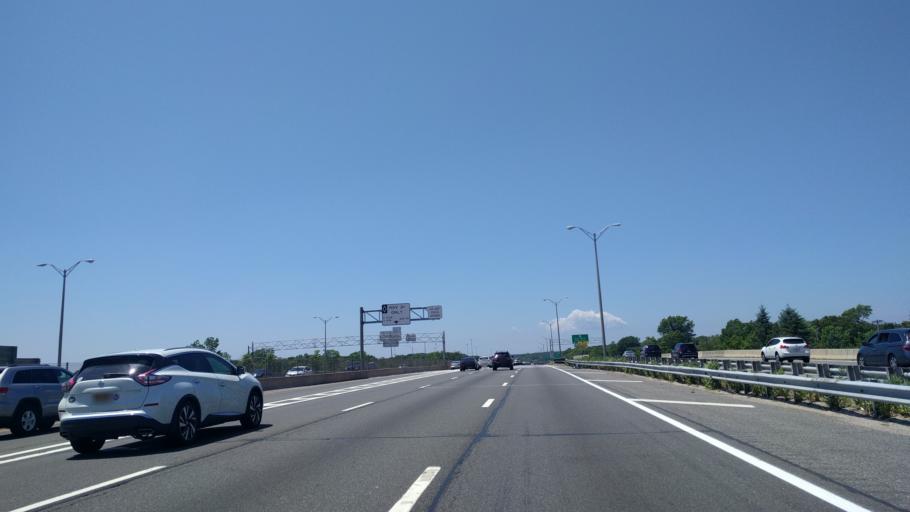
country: US
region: New York
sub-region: Suffolk County
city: Brentwood
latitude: 40.8049
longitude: -73.2677
